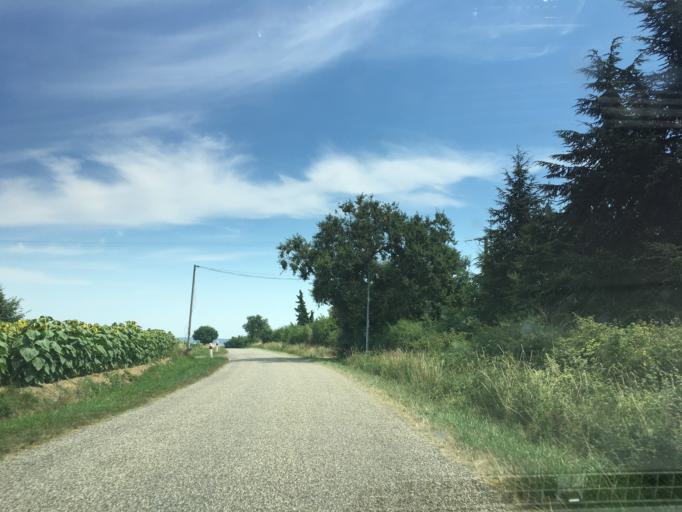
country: FR
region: Midi-Pyrenees
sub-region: Departement du Gers
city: Fleurance
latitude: 43.8163
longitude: 0.6119
